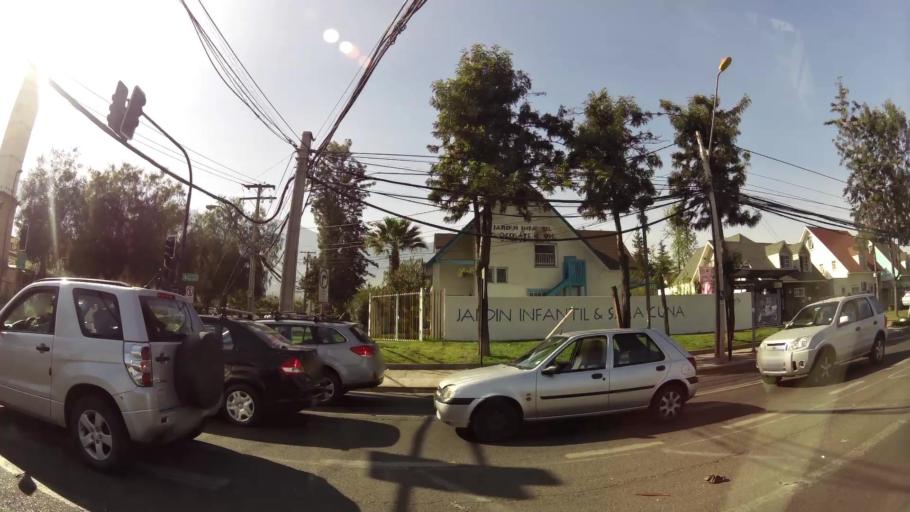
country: CL
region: Santiago Metropolitan
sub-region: Provincia de Santiago
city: Villa Presidente Frei, Nunoa, Santiago, Chile
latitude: -33.4836
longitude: -70.5469
